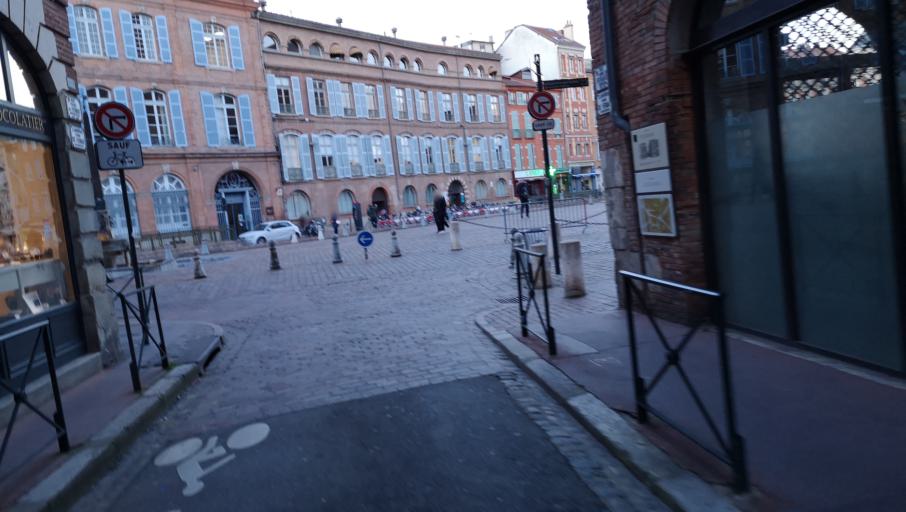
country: FR
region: Midi-Pyrenees
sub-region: Departement de la Haute-Garonne
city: Toulouse
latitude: 43.5994
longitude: 1.4493
